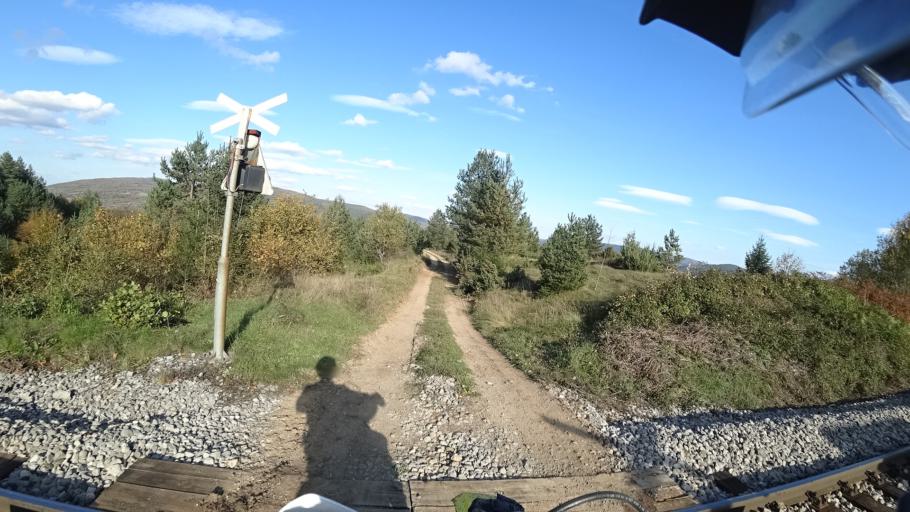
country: HR
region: Karlovacka
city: Plaski
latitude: 44.9975
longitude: 15.4084
